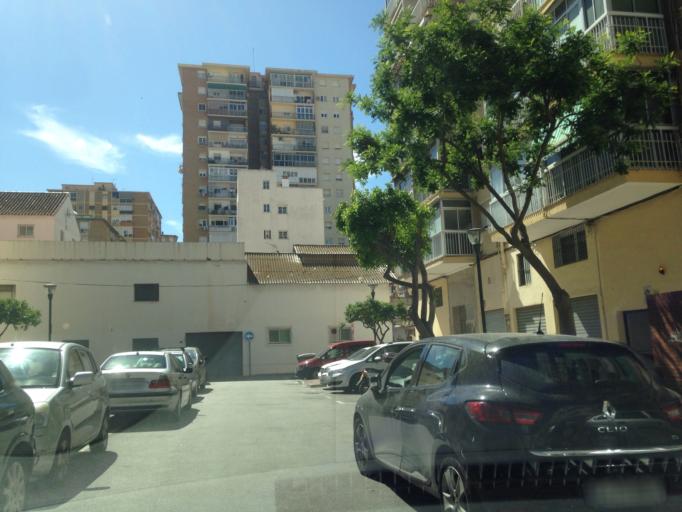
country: ES
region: Andalusia
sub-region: Provincia de Malaga
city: Malaga
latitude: 36.7075
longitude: -4.4374
